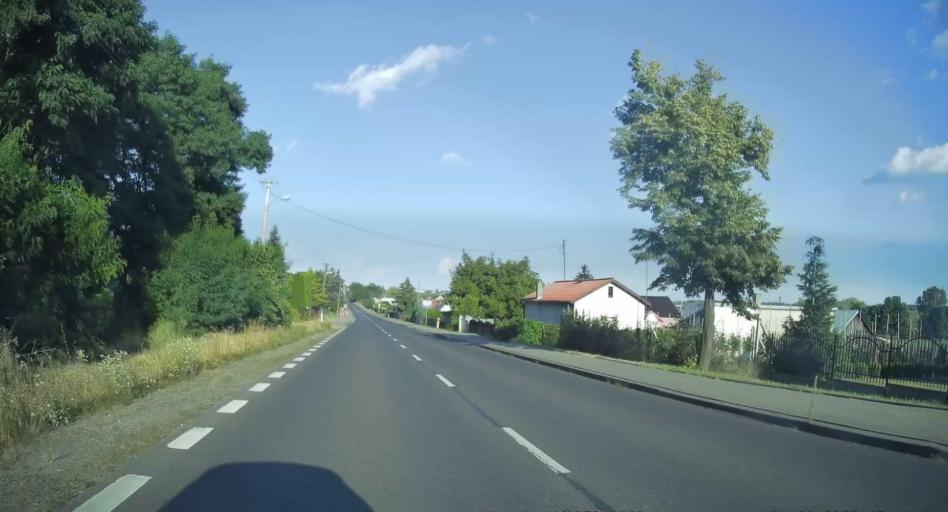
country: PL
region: Lodz Voivodeship
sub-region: Powiat rawski
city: Biala Rawska
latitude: 51.7997
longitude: 20.5187
